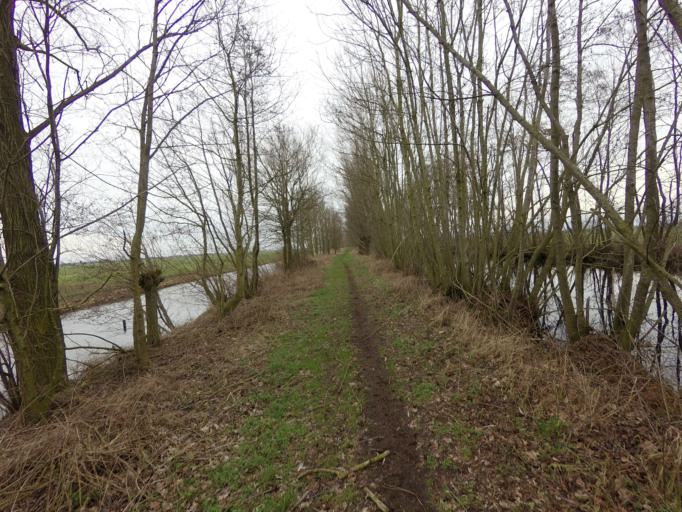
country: NL
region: South Holland
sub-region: Gemeente Vlist
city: Vlist
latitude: 51.9904
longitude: 4.8490
